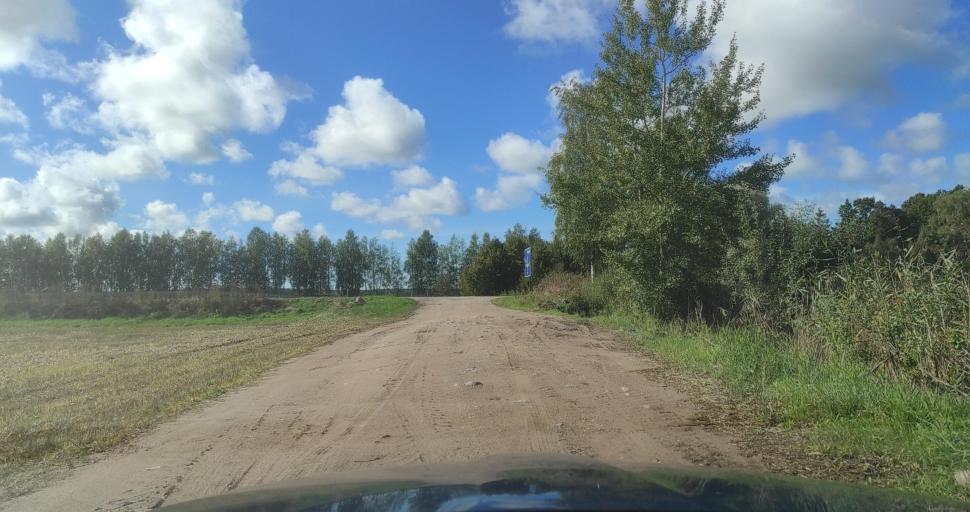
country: LV
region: Ventspils Rajons
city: Piltene
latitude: 57.2725
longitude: 21.5832
